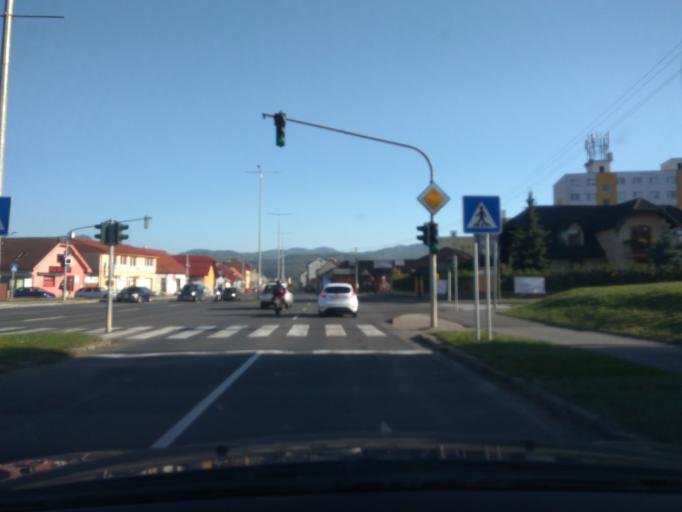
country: SK
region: Banskobystricky
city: Ziar nad Hronom
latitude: 48.5885
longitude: 18.8575
